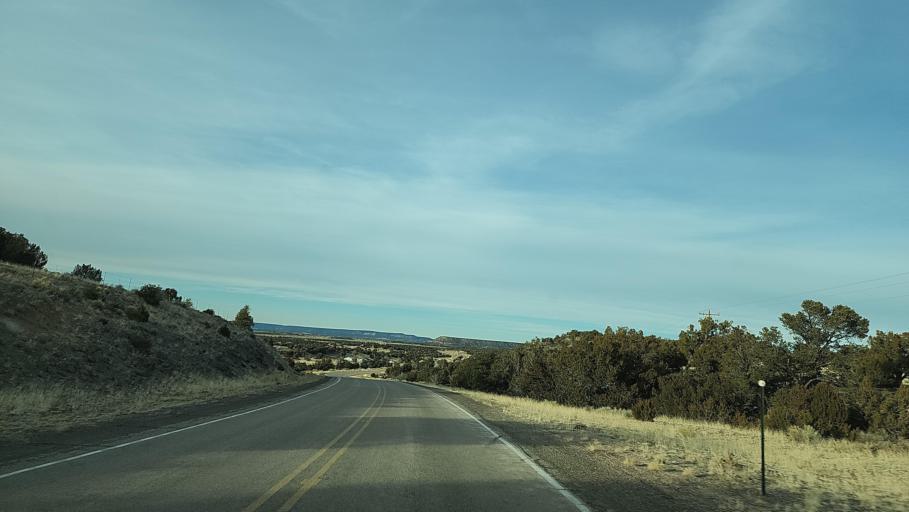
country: US
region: New Mexico
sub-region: McKinley County
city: Black Rock
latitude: 34.4162
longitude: -108.4306
